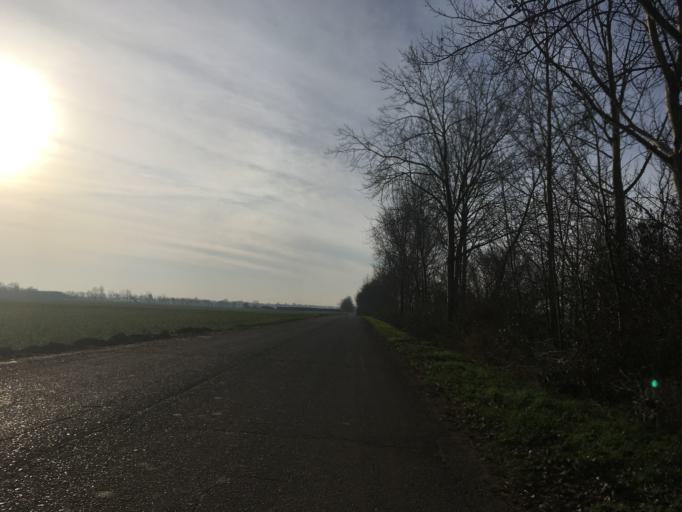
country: DE
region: Brandenburg
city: Wriezen
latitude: 52.7726
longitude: 14.1492
